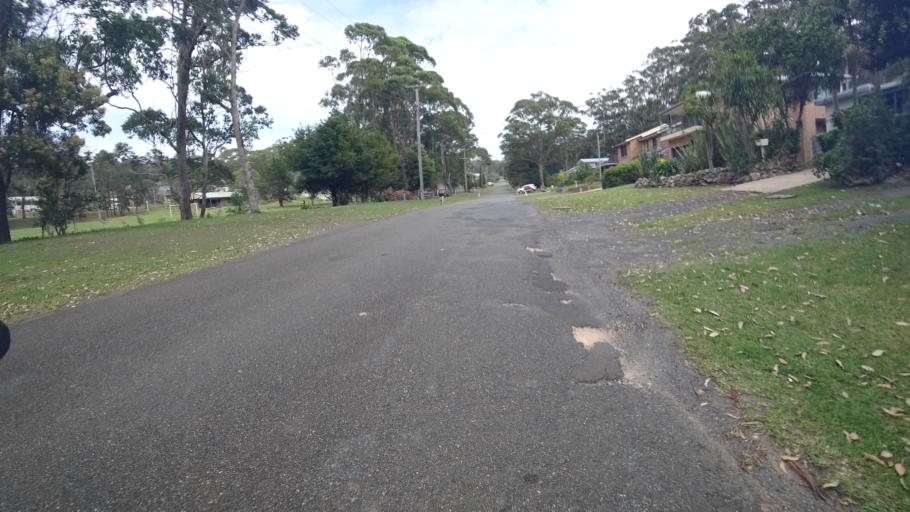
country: AU
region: New South Wales
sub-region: Shoalhaven Shire
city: Milton
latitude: -35.2582
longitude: 150.5122
